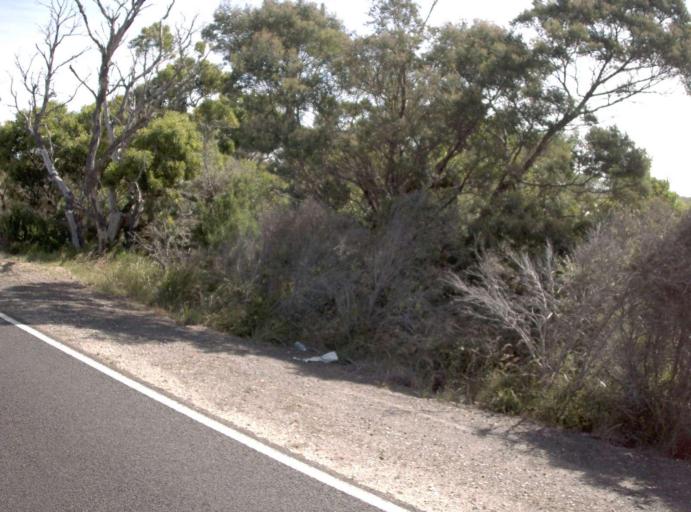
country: AU
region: Victoria
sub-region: Wellington
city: Sale
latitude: -38.3530
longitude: 147.1712
